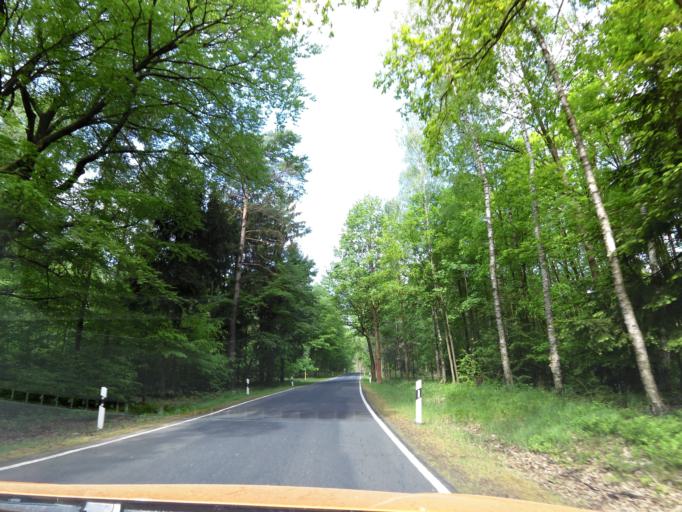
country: DE
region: Brandenburg
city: Wiesenburg
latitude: 52.0824
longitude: 12.4910
